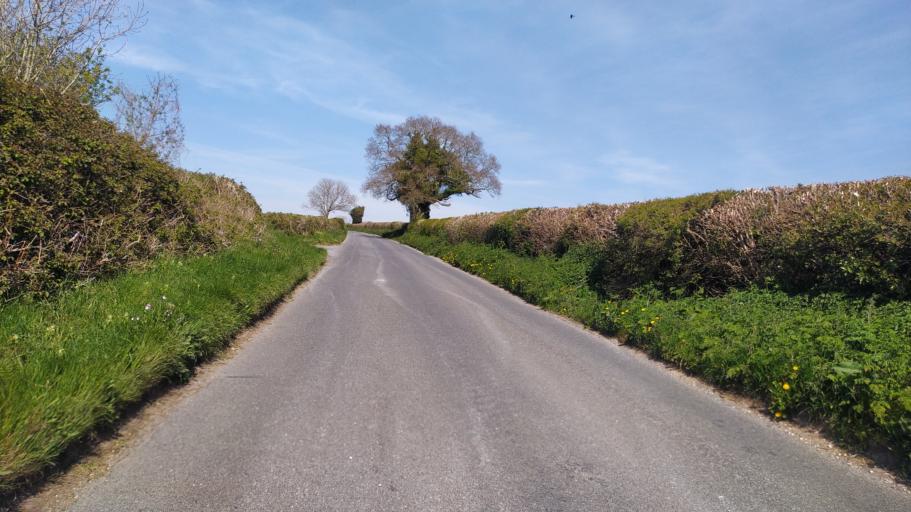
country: GB
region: England
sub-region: Dorset
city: Blandford Forum
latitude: 50.8795
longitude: -2.1902
